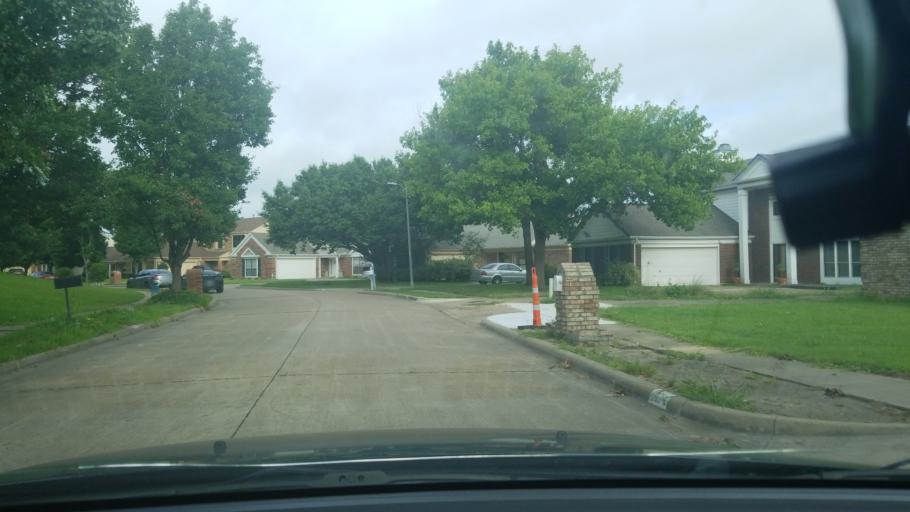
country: US
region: Texas
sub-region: Dallas County
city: Mesquite
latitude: 32.7893
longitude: -96.6495
